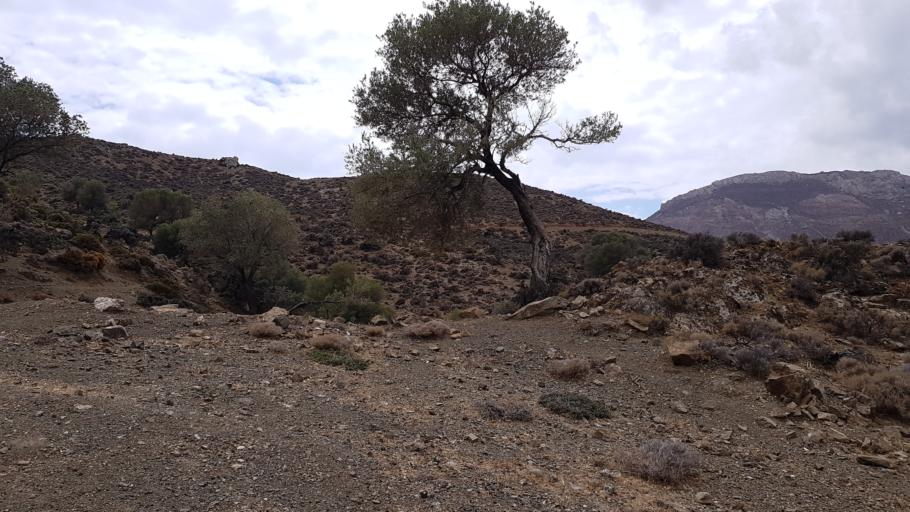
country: GR
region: Crete
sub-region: Nomos Irakleiou
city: Agioi Deka
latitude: 34.9443
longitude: 24.9919
